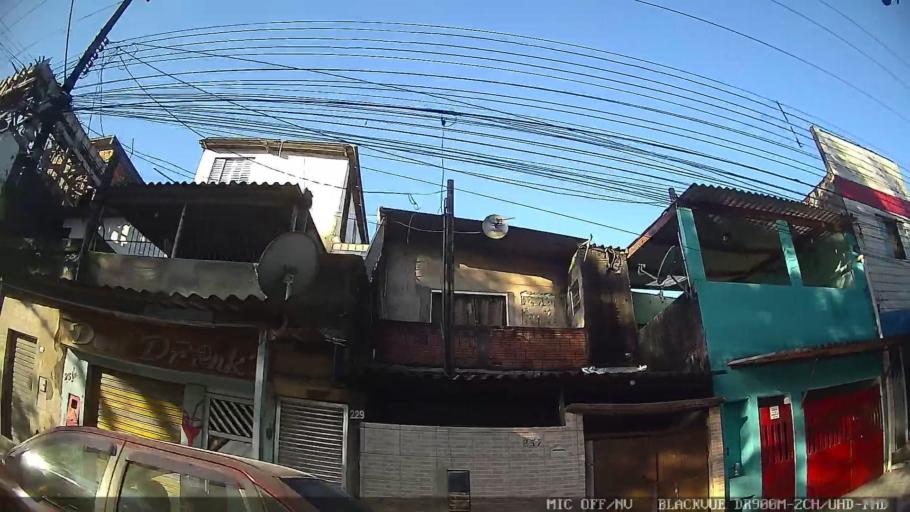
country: BR
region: Sao Paulo
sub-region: Guaruja
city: Guaruja
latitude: -23.9614
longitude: -46.2500
